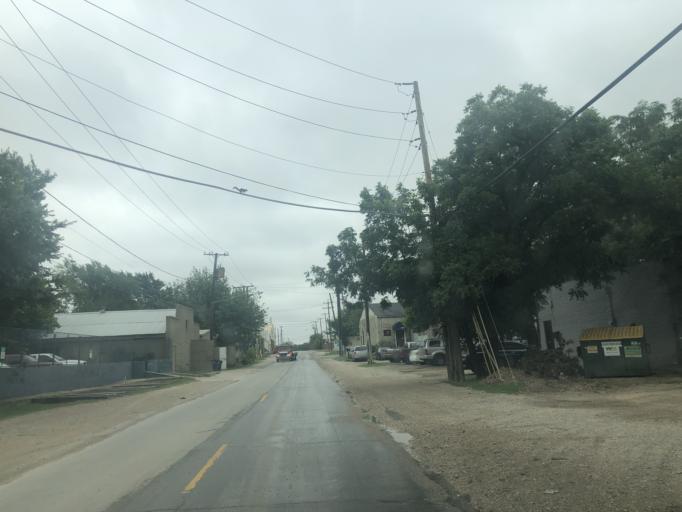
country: US
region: Texas
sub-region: Dallas County
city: Dallas
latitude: 32.7727
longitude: -96.8491
